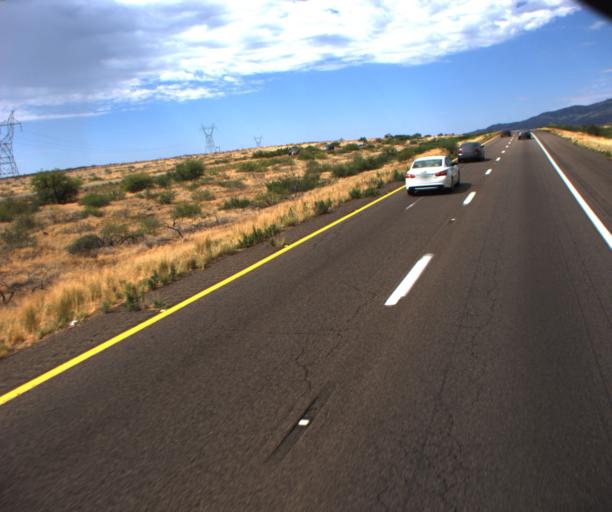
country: US
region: Arizona
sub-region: Yavapai County
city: Cordes Lakes
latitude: 34.2135
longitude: -112.1140
